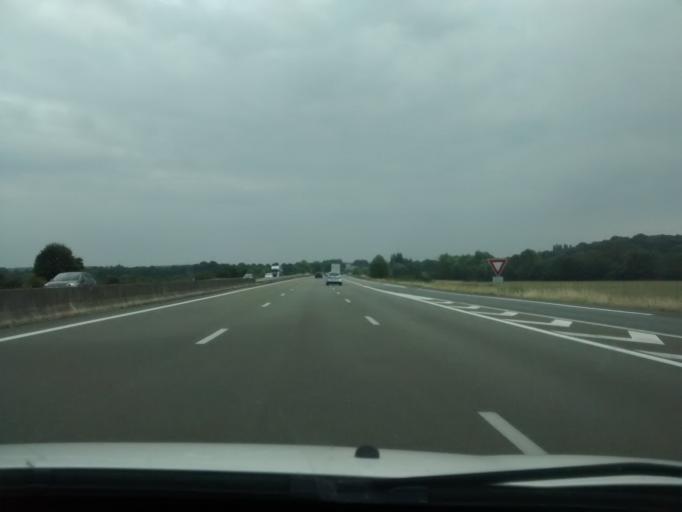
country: FR
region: Pays de la Loire
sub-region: Departement de la Sarthe
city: Neuville-sur-Sarthe
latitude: 48.0566
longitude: 0.1946
